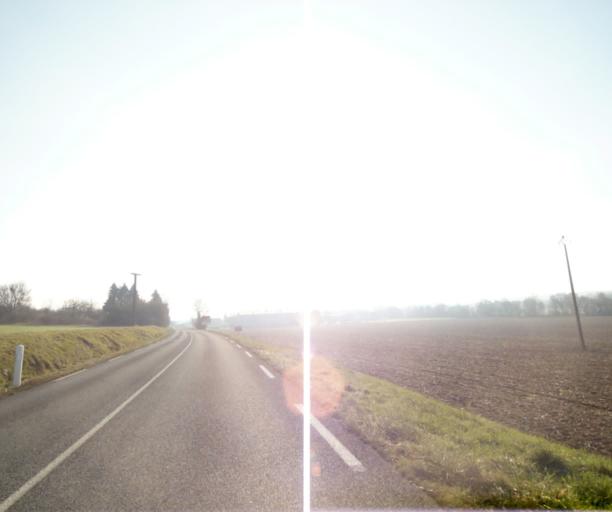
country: FR
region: Champagne-Ardenne
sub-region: Departement de la Haute-Marne
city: Wassy
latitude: 48.5085
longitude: 4.9405
